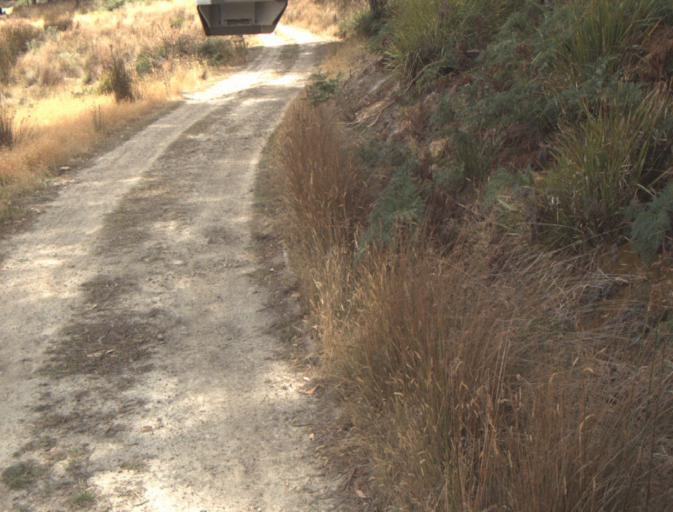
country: AU
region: Tasmania
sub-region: Launceston
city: Mayfield
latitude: -41.2090
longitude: 147.1574
